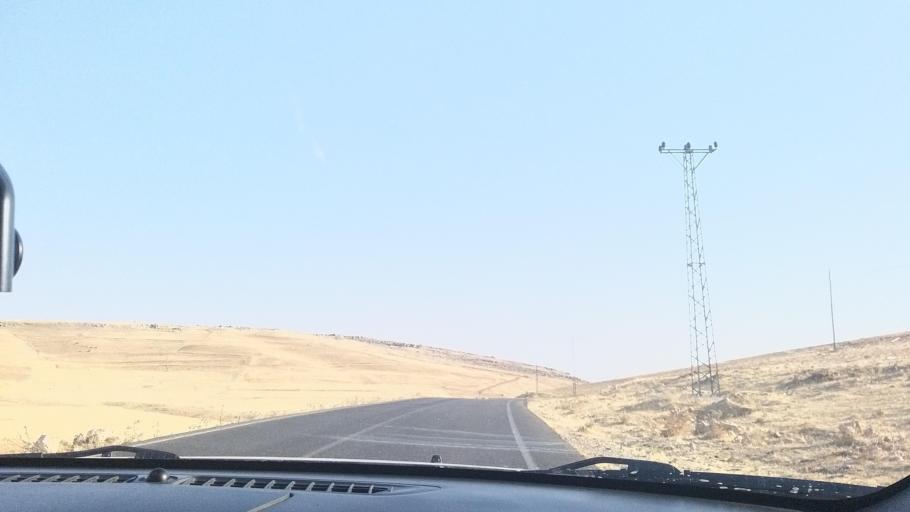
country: TR
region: Diyarbakir
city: Silvan
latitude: 38.1739
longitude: 41.0050
